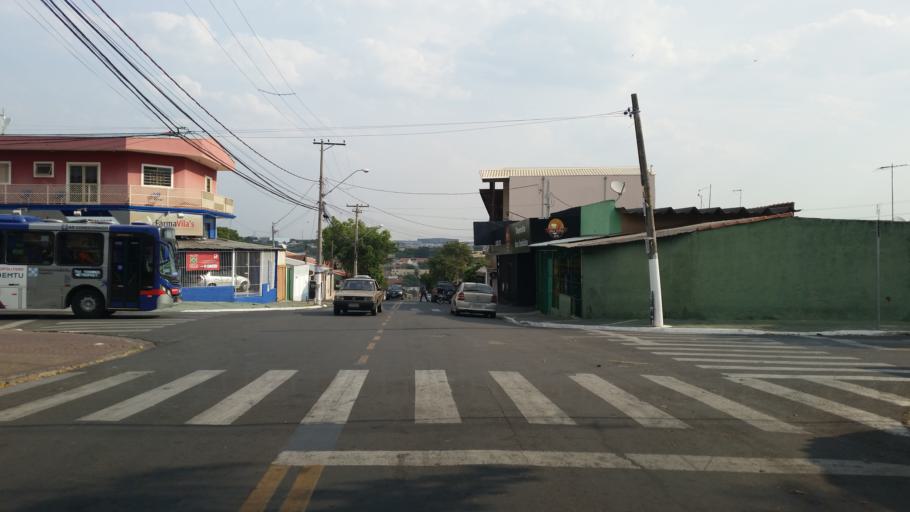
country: BR
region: Sao Paulo
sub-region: Hortolandia
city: Hortolandia
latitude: -22.8823
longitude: -47.1765
